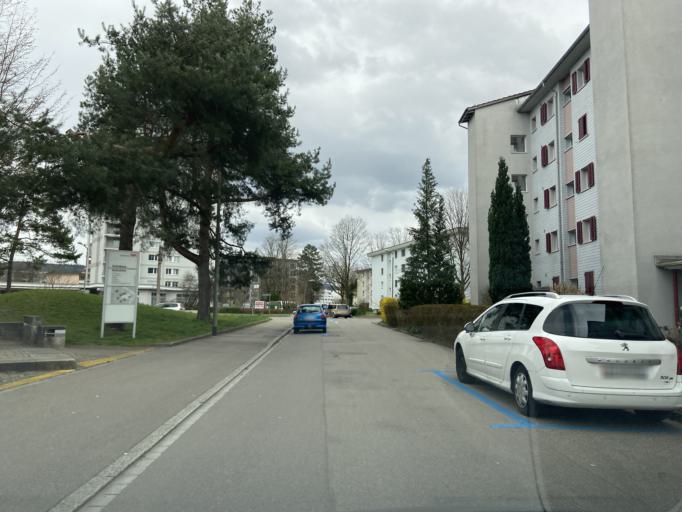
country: CH
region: Zurich
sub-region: Bezirk Winterthur
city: Mattenbach (Kreis 7) / Endliker
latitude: 47.4912
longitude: 8.7483
